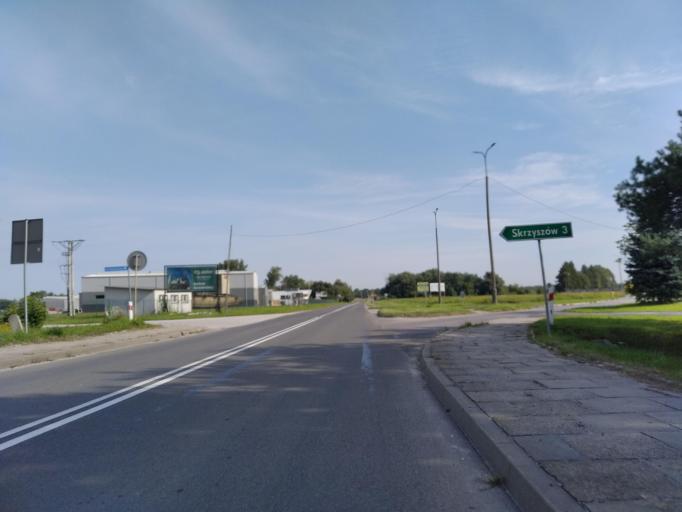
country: PL
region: Subcarpathian Voivodeship
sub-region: Powiat ropczycko-sedziszowski
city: Ostrow
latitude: 50.0861
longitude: 21.5884
